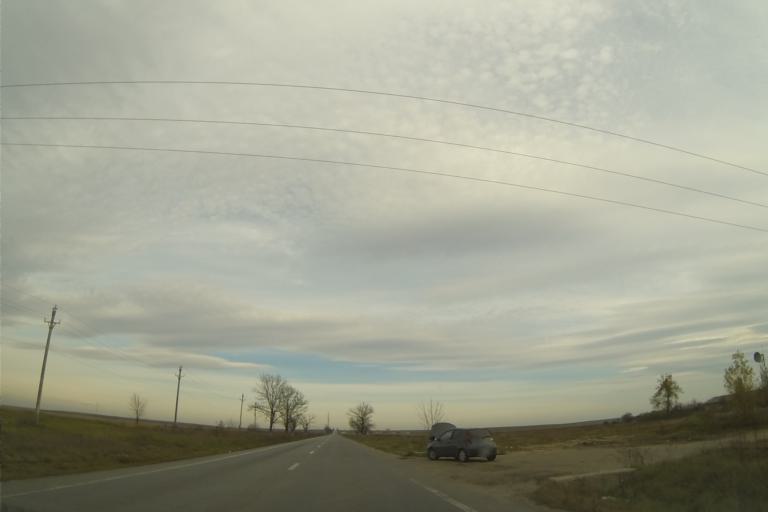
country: RO
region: Olt
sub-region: Comuna Valea Mare
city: Valea Mare
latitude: 44.4642
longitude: 24.4109
